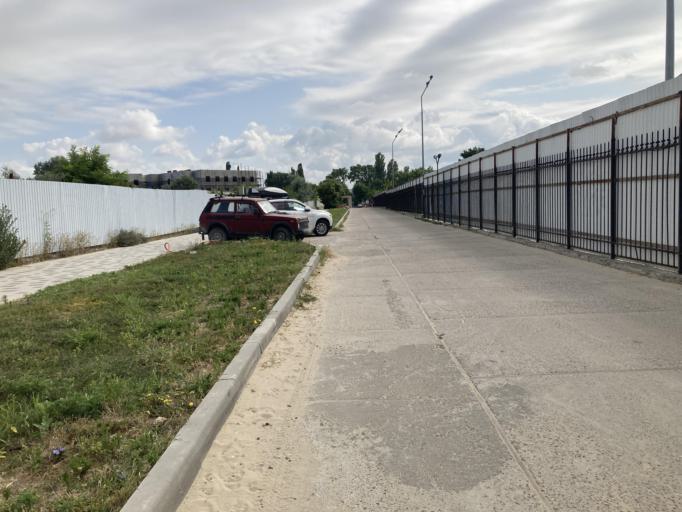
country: RU
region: Krasnodarskiy
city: Anapa
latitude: 44.9397
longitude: 37.3053
